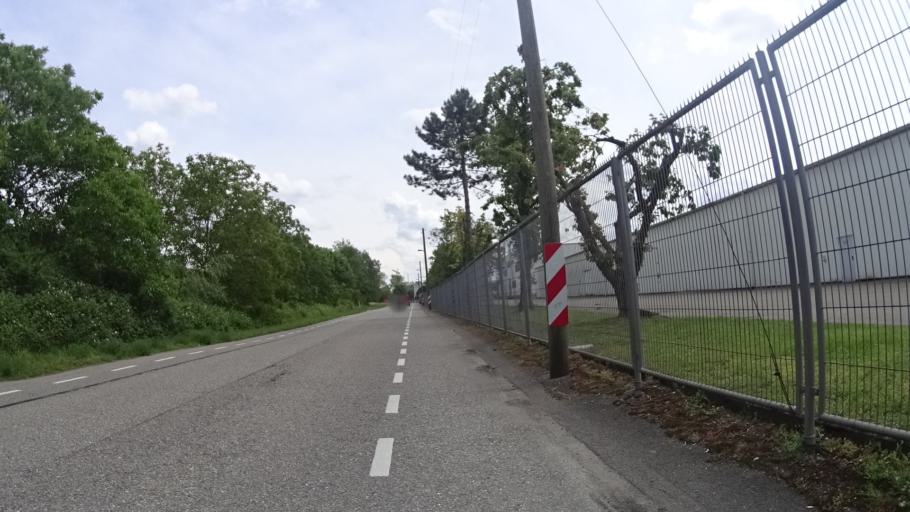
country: CH
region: Basel-City
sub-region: Basel-Stadt
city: Bettingen
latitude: 47.5515
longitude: 7.6543
